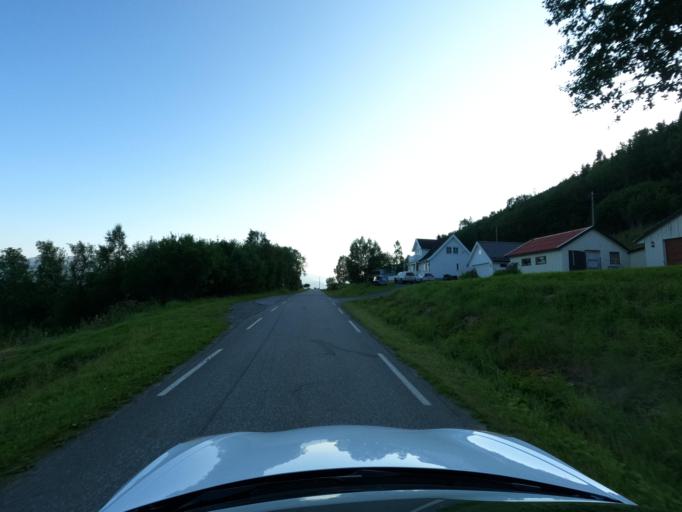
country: NO
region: Nordland
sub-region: Ballangen
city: Ballangen
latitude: 68.4657
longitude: 16.7813
